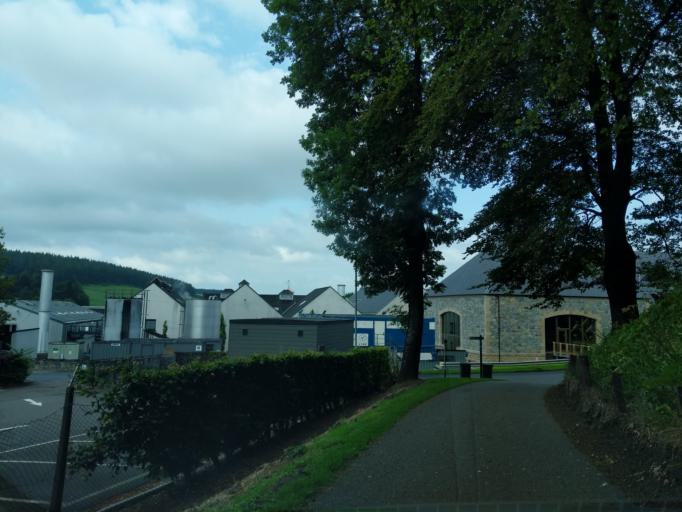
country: GB
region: Scotland
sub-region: Moray
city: Dufftown
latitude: 57.4533
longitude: -3.1261
